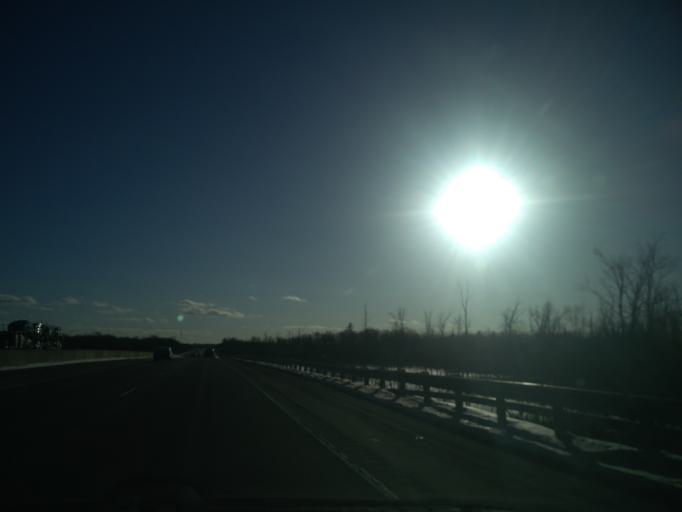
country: CA
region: Ontario
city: Prescott
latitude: 44.7363
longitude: -75.5058
